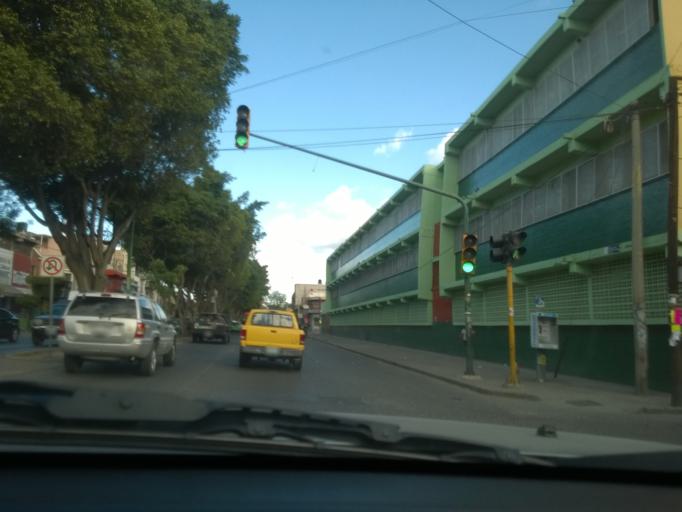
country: MX
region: Guanajuato
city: Leon
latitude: 21.1313
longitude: -101.6644
